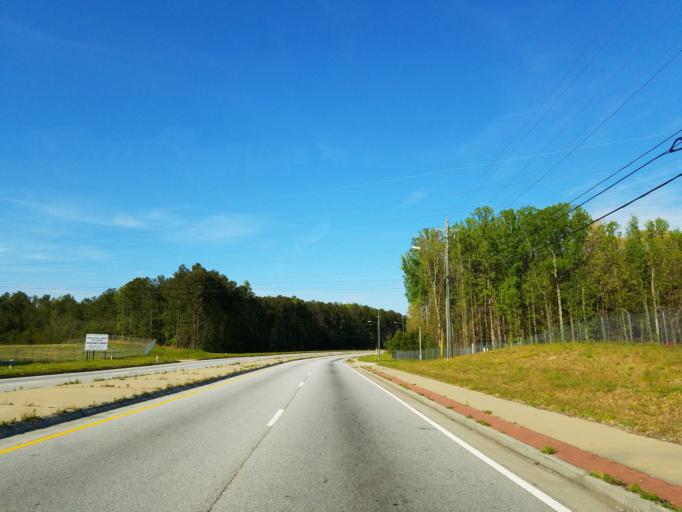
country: US
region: Georgia
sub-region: Cobb County
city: Mableton
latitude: 33.7866
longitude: -84.5035
